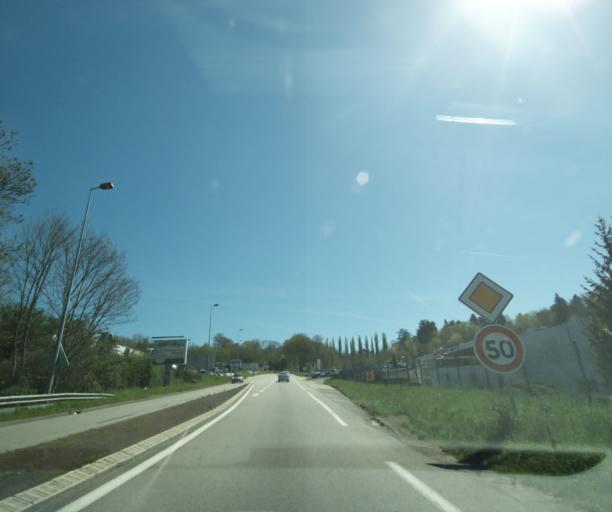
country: FR
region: Limousin
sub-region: Departement de la Haute-Vienne
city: Condat-sur-Vienne
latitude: 45.8029
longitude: 1.2928
